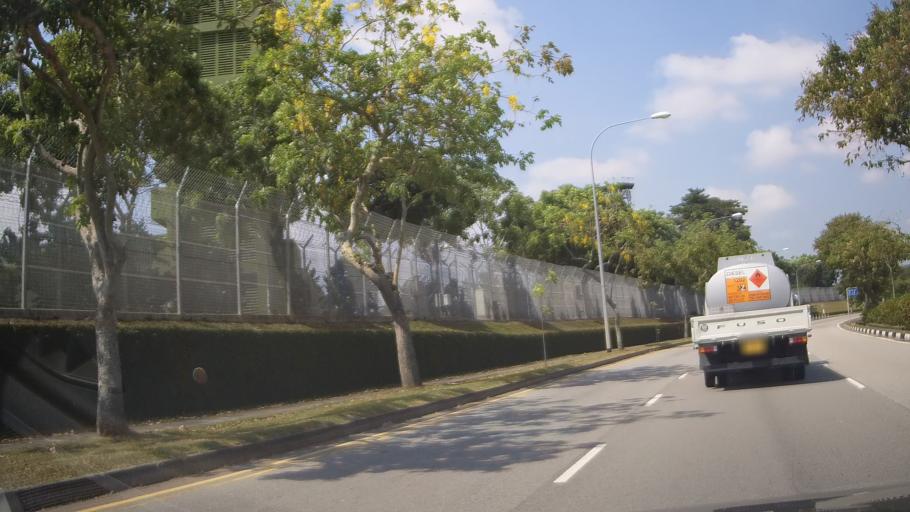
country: SG
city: Singapore
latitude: 1.3642
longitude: 103.9081
